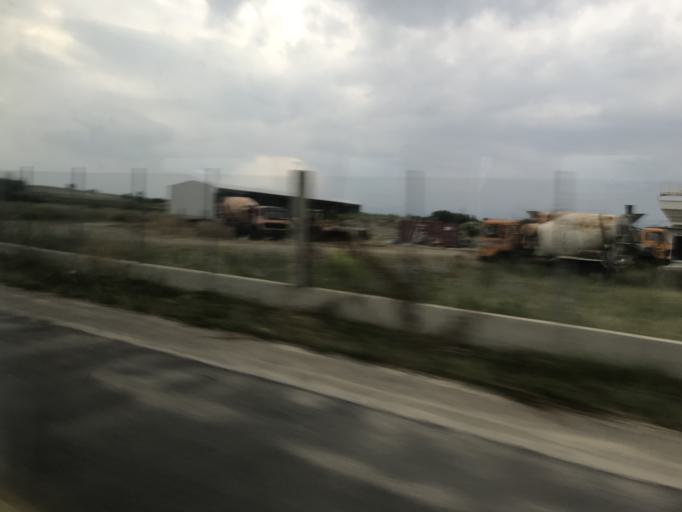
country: GR
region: East Macedonia and Thrace
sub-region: Nomos Rodopis
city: Aratos
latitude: 41.0870
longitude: 25.5163
